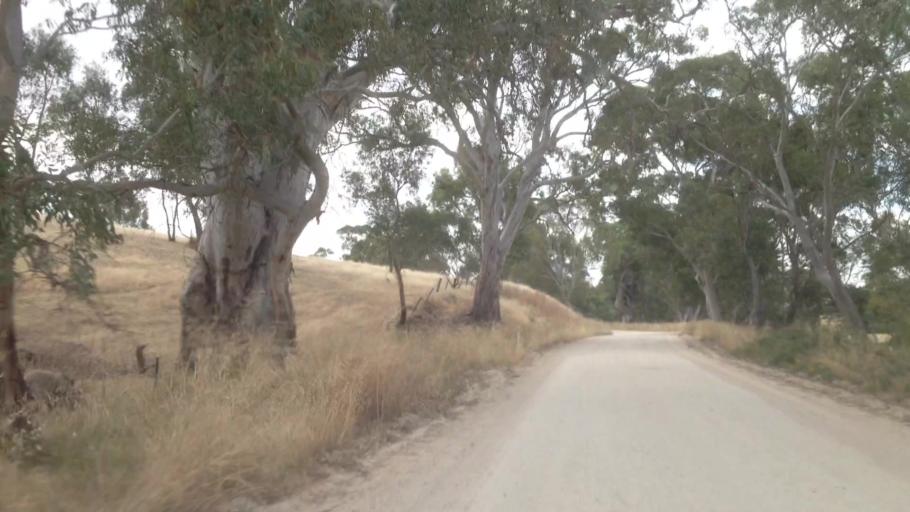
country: AU
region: South Australia
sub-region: Barossa
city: Lyndoch
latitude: -34.6017
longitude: 138.9473
